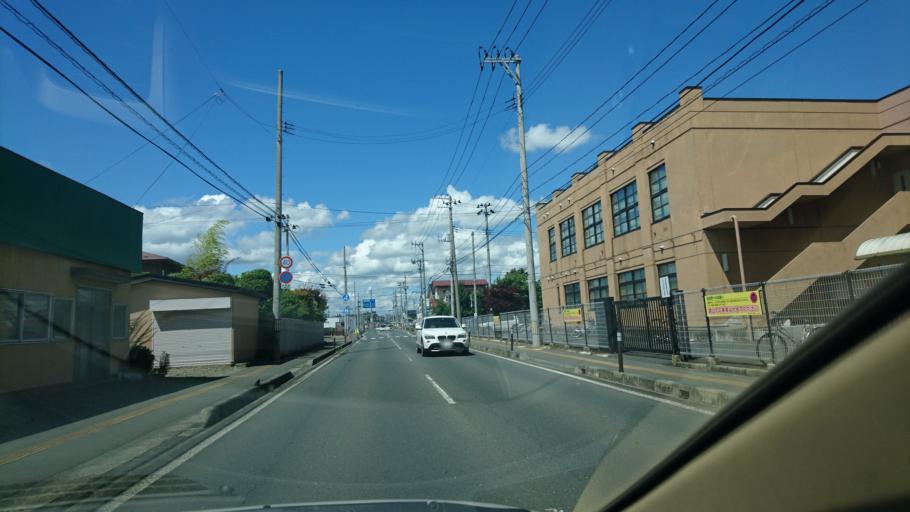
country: JP
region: Iwate
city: Kitakami
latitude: 39.2908
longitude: 141.1097
